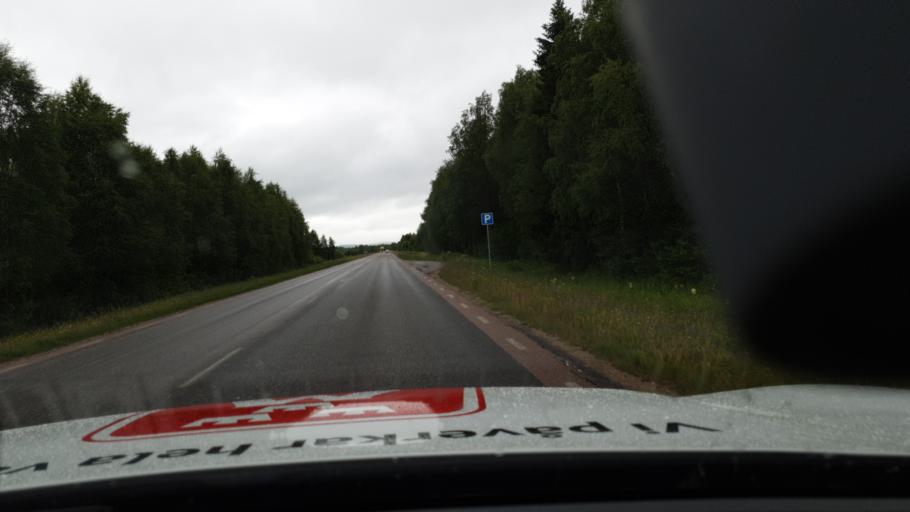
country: SE
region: Norrbotten
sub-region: Overtornea Kommun
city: OEvertornea
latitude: 66.4090
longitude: 23.6238
